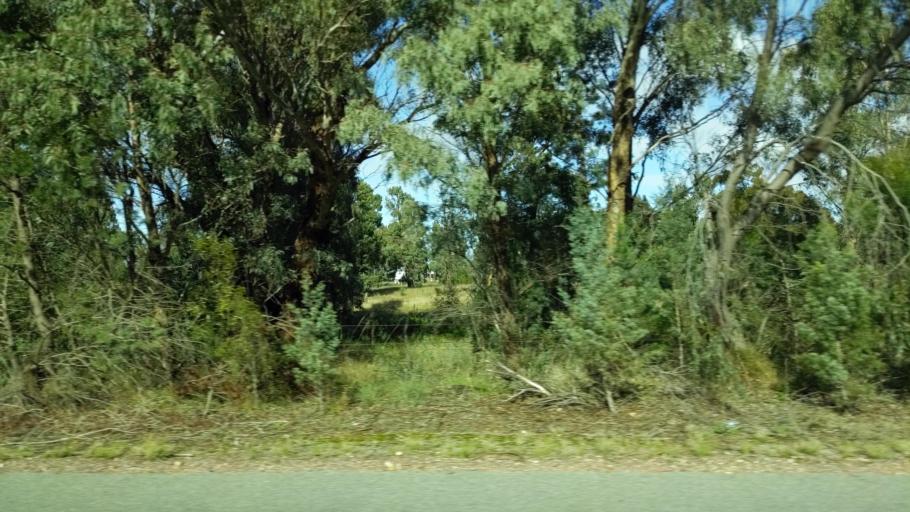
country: AU
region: New South Wales
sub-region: Narrandera
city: Narrandera
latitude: -34.7459
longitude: 146.8132
